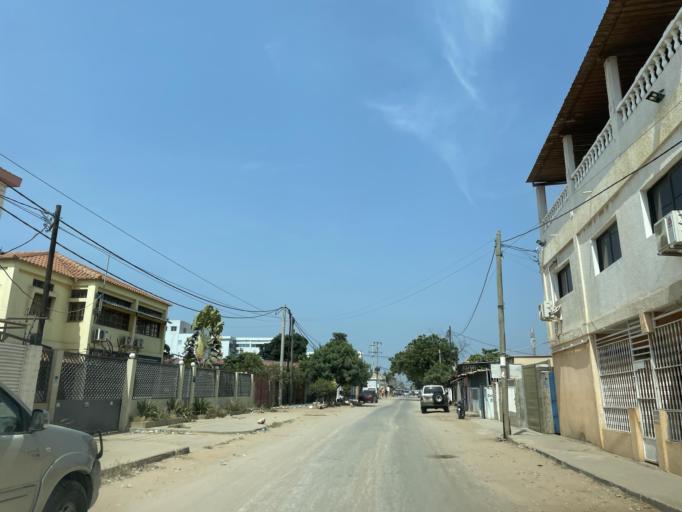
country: AO
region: Luanda
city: Luanda
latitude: -8.9000
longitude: 13.1839
